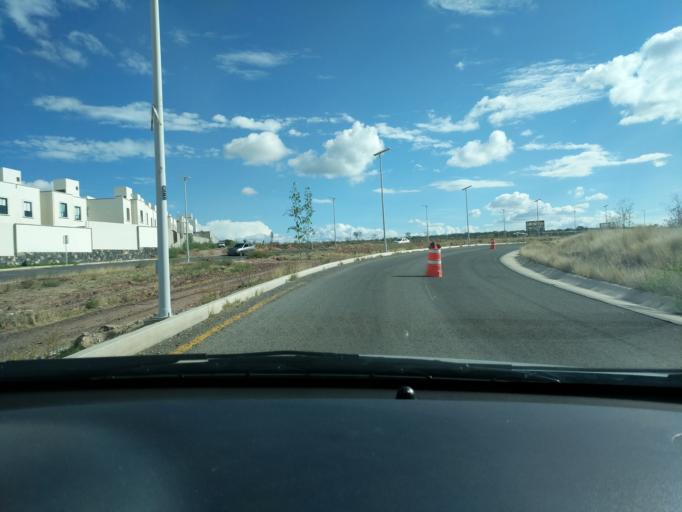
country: MX
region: Queretaro
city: La Canada
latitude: 20.5975
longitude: -100.2938
